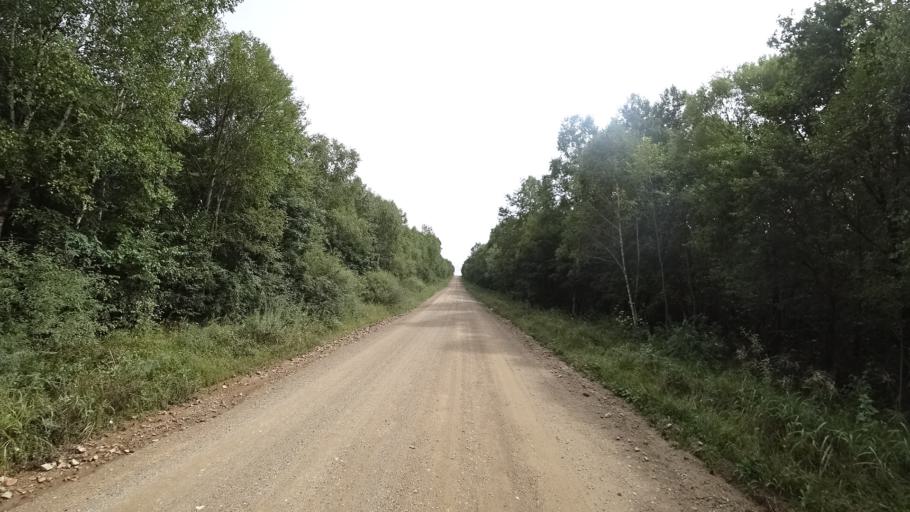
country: RU
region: Primorskiy
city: Lyalichi
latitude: 44.0974
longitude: 132.4295
